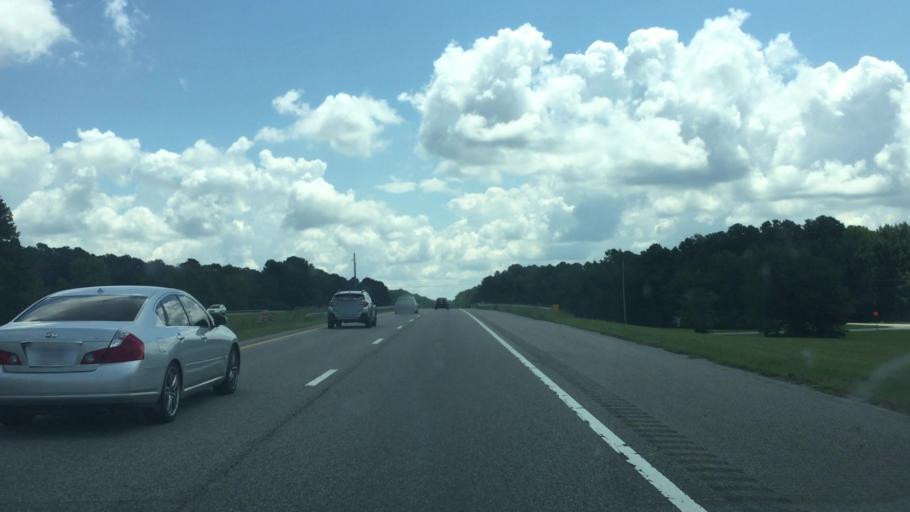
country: US
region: North Carolina
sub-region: Robeson County
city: Lumberton
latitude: 34.5804
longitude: -79.0499
